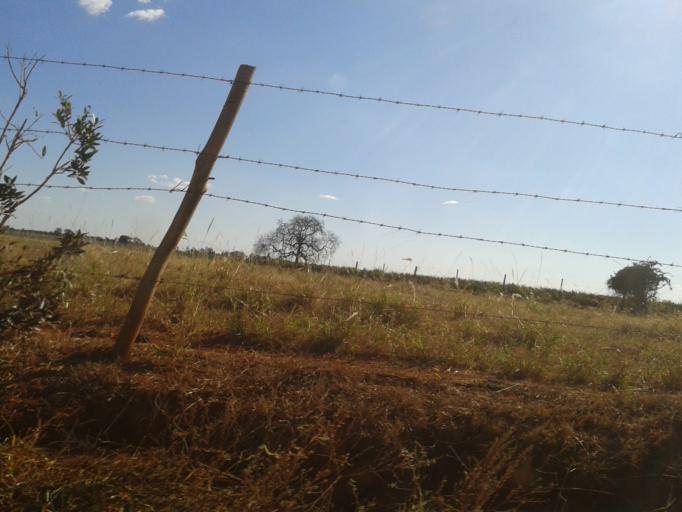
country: BR
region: Minas Gerais
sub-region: Centralina
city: Centralina
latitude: -18.7481
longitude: -49.1874
